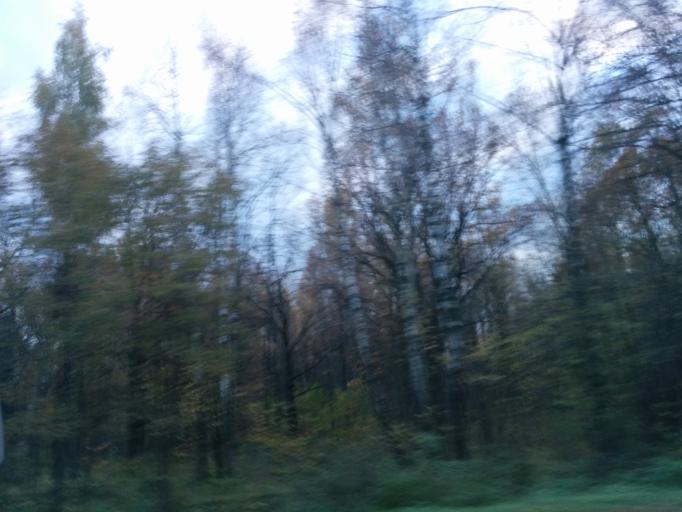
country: RU
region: Moskovskaya
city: Biryulevo Zapadnoye
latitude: 55.5401
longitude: 37.6312
